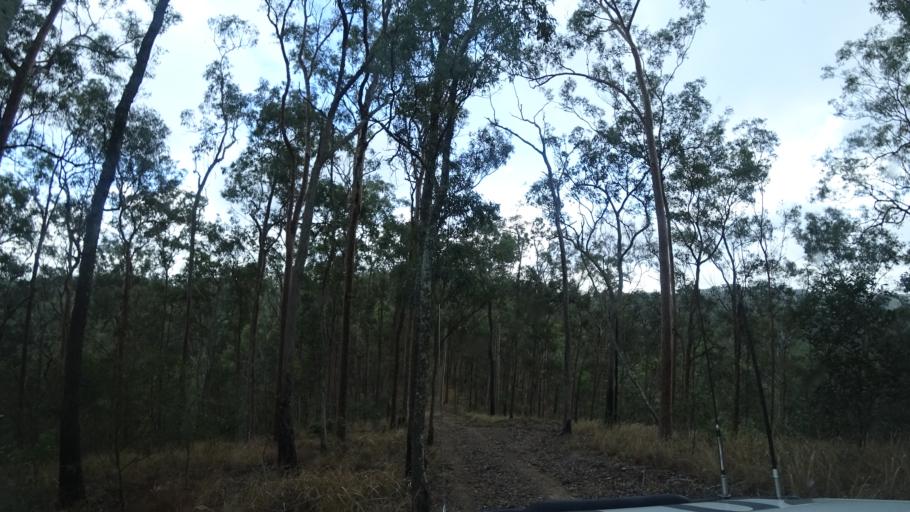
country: AU
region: Queensland
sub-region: Brisbane
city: Pullenvale
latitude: -27.4616
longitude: 152.8661
